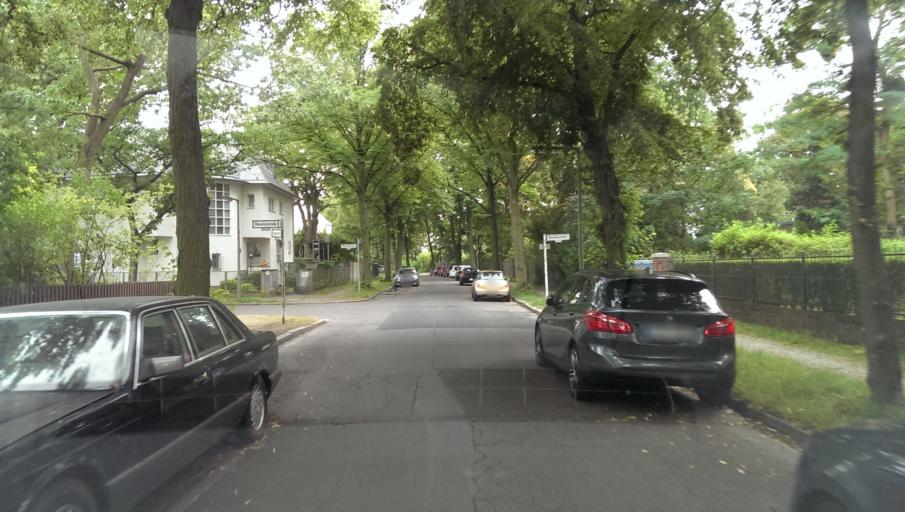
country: DE
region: Berlin
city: Zehlendorf Bezirk
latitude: 52.4474
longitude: 13.2619
